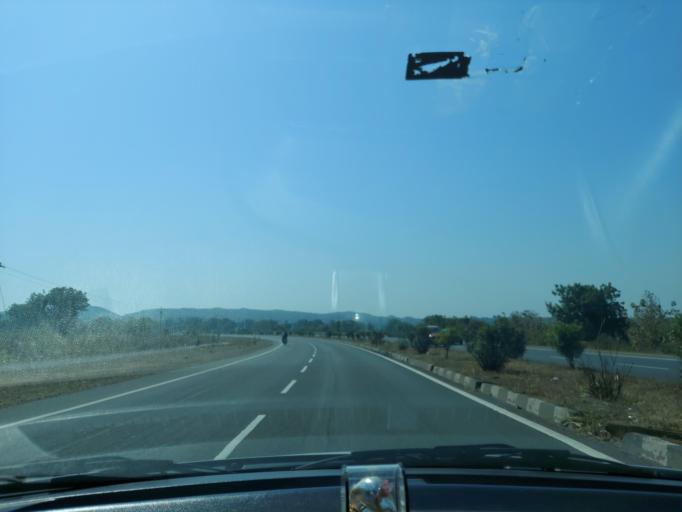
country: IN
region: Madhya Pradesh
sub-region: Dhar
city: Dhamnod
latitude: 22.3260
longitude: 75.4969
